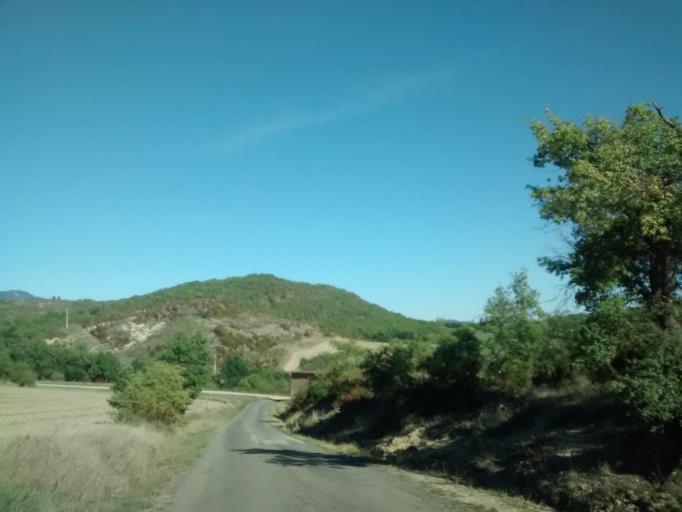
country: ES
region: Aragon
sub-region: Provincia de Huesca
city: Santa Cruz de la Seros
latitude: 42.4361
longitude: -0.6550
